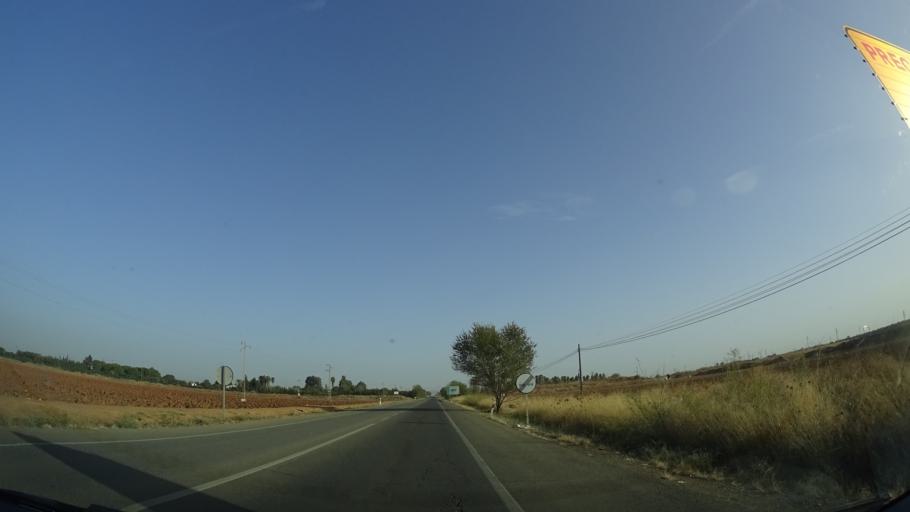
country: ES
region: Andalusia
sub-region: Provincia de Sevilla
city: La Algaba
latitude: 37.4375
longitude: -5.9790
